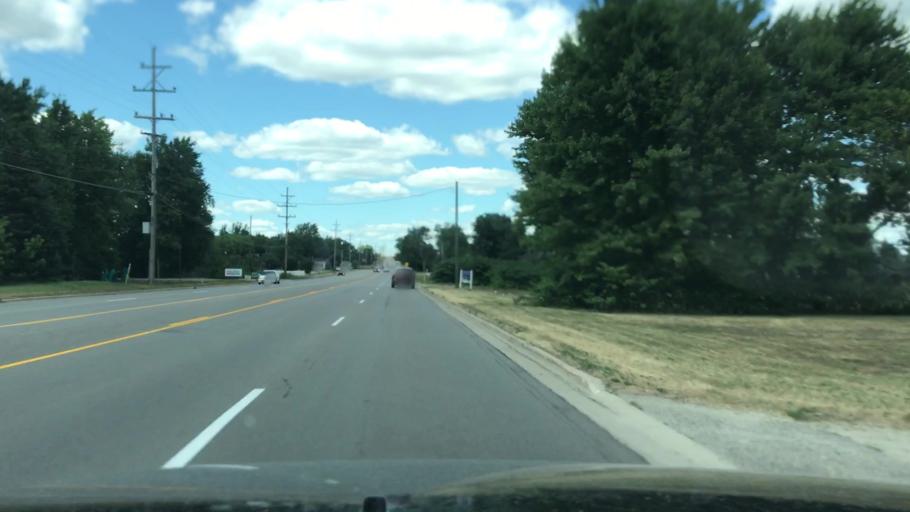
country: US
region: Michigan
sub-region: Kent County
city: Byron Center
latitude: 42.8373
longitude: -85.7230
